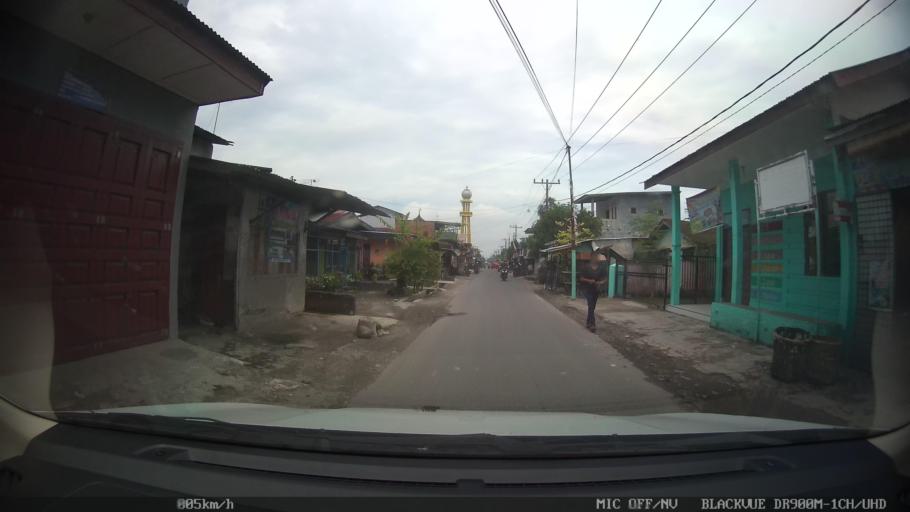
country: ID
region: North Sumatra
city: Sunggal
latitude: 3.6000
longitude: 98.5541
